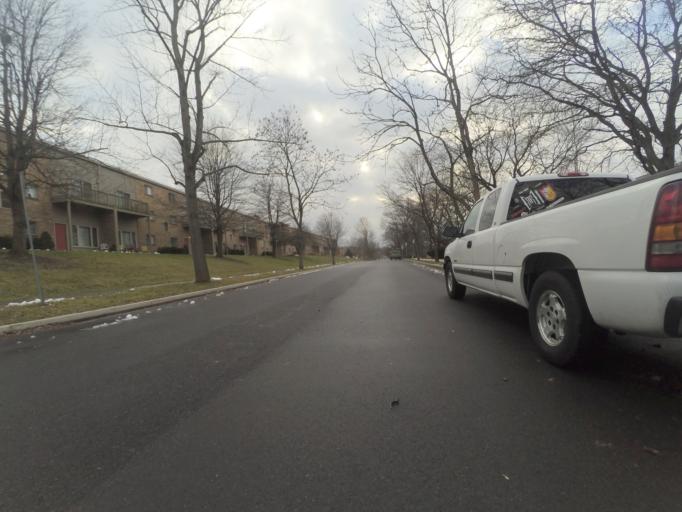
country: US
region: Pennsylvania
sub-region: Centre County
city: State College
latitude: 40.8027
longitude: -77.8438
